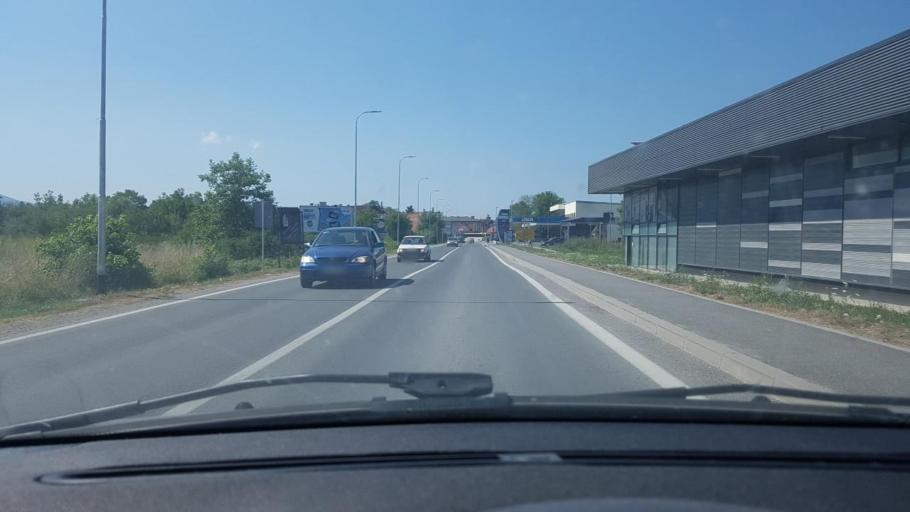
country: BA
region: Federation of Bosnia and Herzegovina
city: Bihac
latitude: 44.8125
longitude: 15.8801
